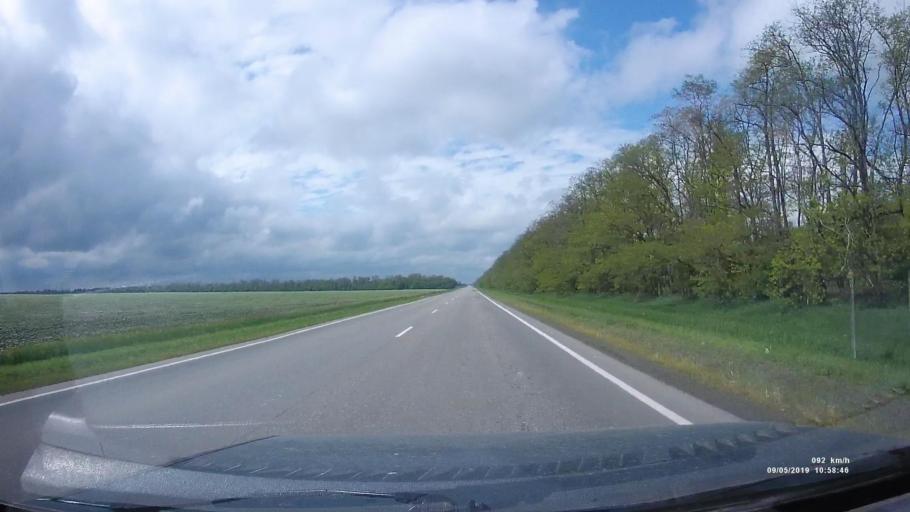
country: RU
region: Rostov
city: Peshkovo
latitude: 46.8606
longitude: 39.2533
